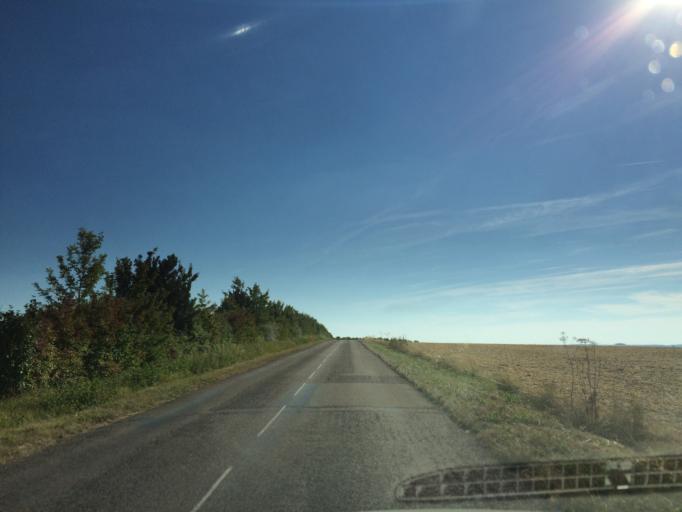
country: FR
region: Bourgogne
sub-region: Departement de l'Yonne
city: Cheny
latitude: 47.9238
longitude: 3.5013
